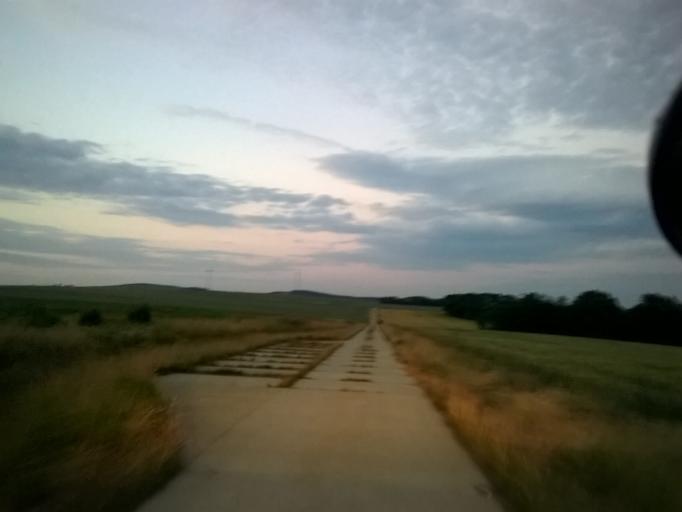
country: SK
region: Trnavsky
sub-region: Okres Senica
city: Senica
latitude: 48.7362
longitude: 17.3236
